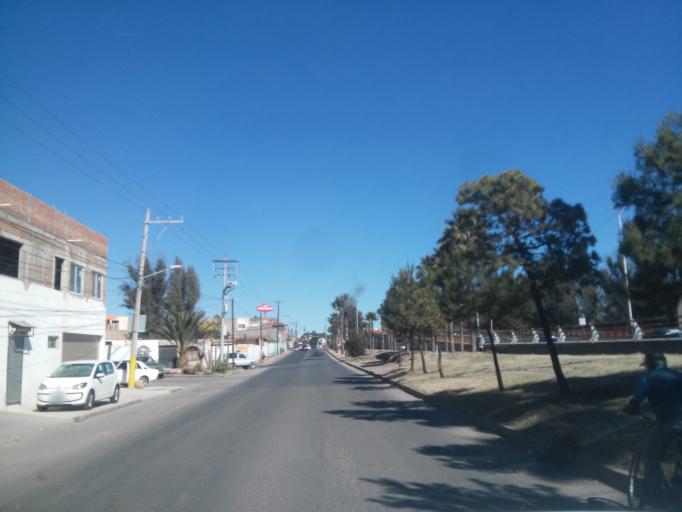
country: MX
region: Durango
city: Victoria de Durango
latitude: 24.0280
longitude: -104.6895
